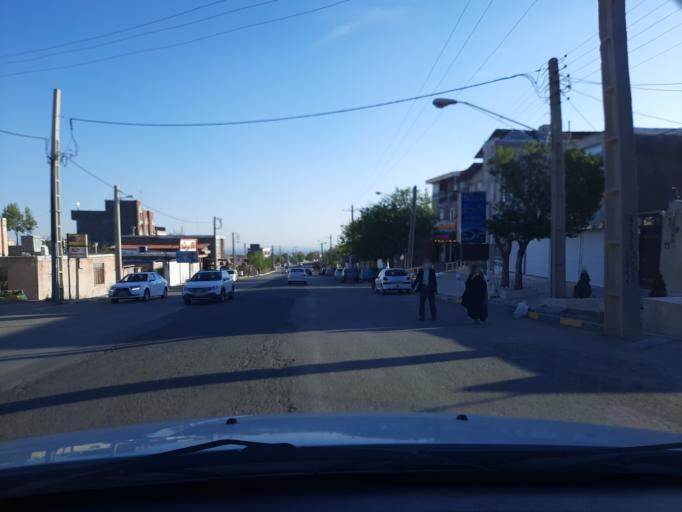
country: IR
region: Qazvin
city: Qazvin
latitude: 36.3329
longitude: 50.1514
